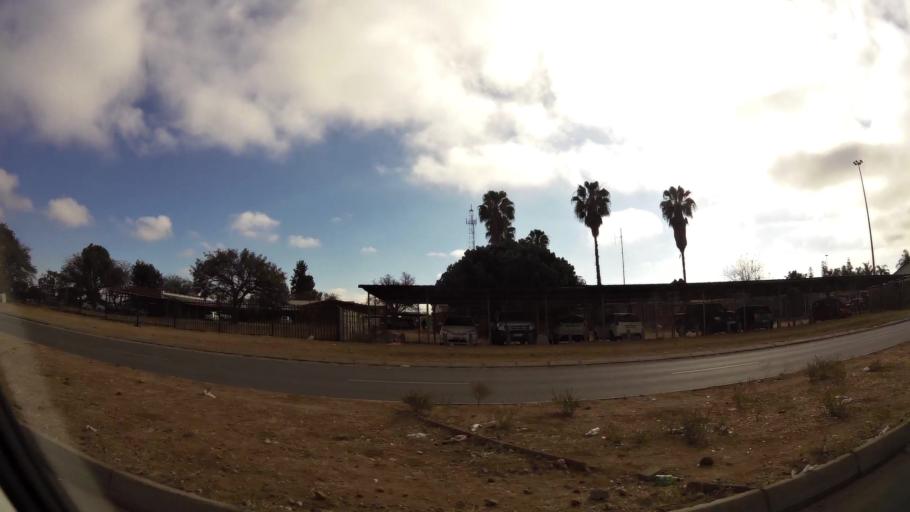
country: ZA
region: Limpopo
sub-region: Capricorn District Municipality
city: Polokwane
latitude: -23.8547
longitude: 29.3811
